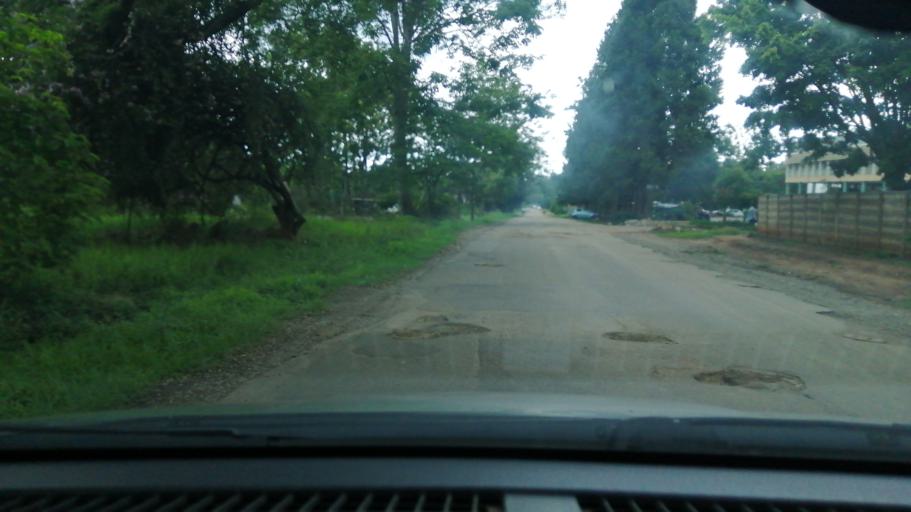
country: ZW
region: Harare
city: Harare
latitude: -17.7731
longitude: 31.0998
